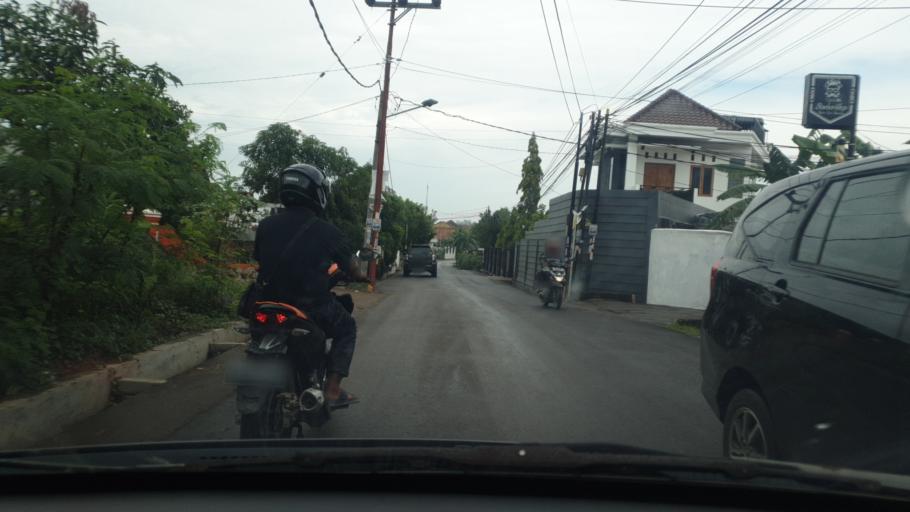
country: ID
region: South Sumatra
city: Palembang
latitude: -2.9738
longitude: 104.7206
